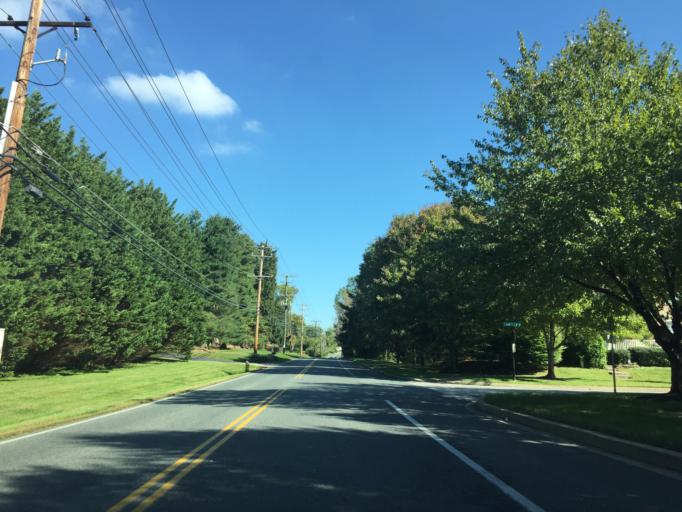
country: US
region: Maryland
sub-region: Harford County
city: Bel Air North
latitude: 39.5755
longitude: -76.3605
